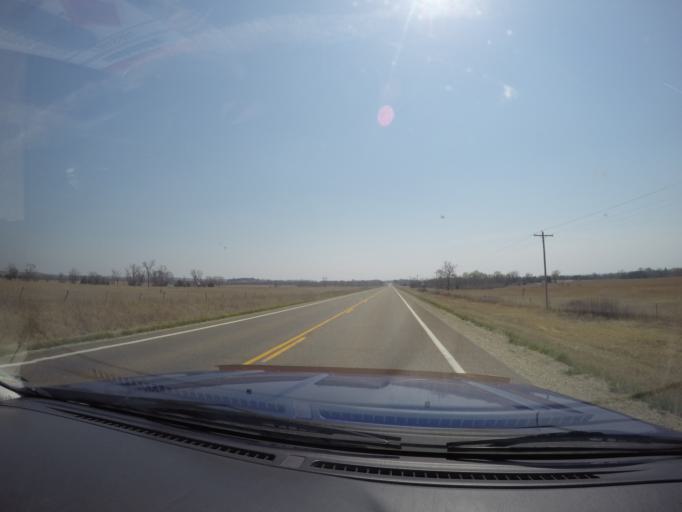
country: US
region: Kansas
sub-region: Morris County
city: Council Grove
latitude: 38.7127
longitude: -96.4974
